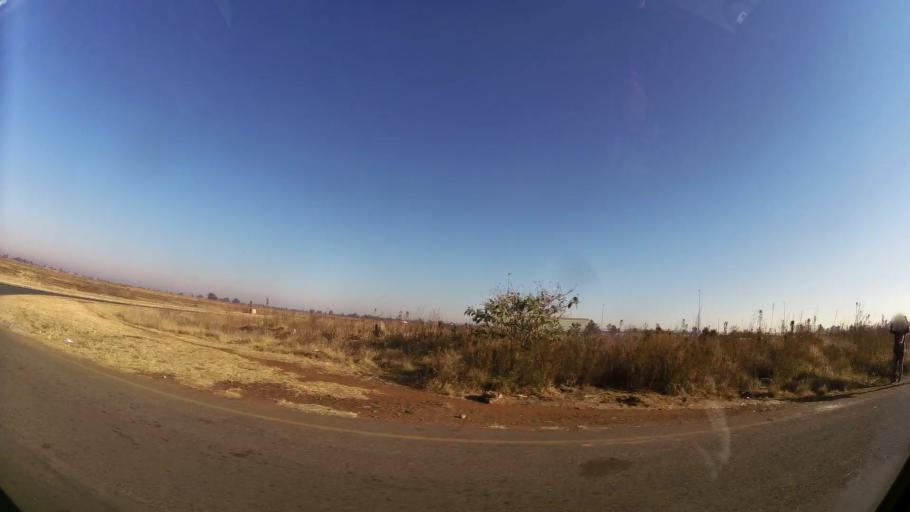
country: ZA
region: Gauteng
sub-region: Ekurhuleni Metropolitan Municipality
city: Germiston
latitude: -26.3334
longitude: 28.1370
